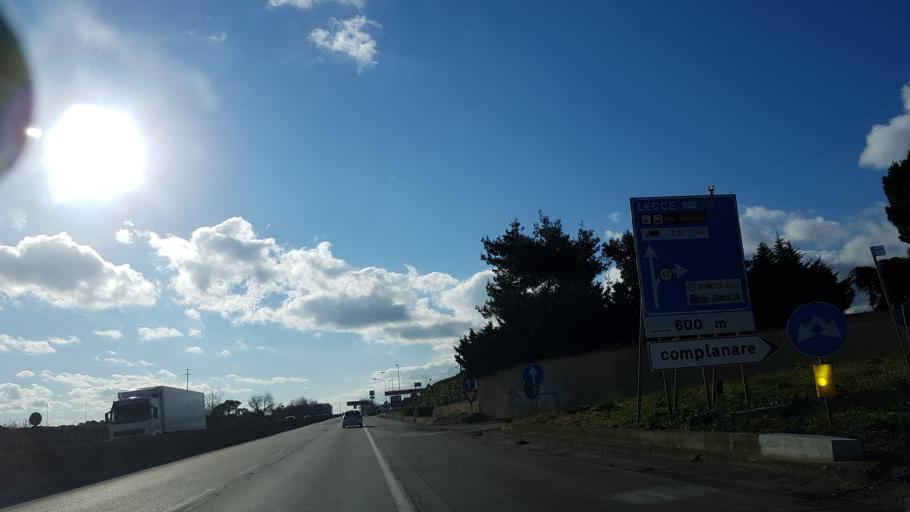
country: IT
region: Apulia
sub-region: Provincia di Brindisi
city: Brindisi
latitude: 40.6346
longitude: 17.9167
